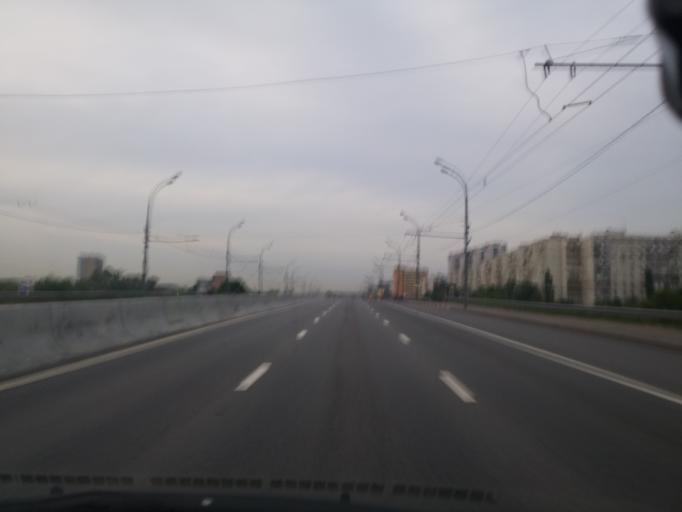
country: RU
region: Moscow
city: Slobodka
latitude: 55.8685
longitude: 37.5849
